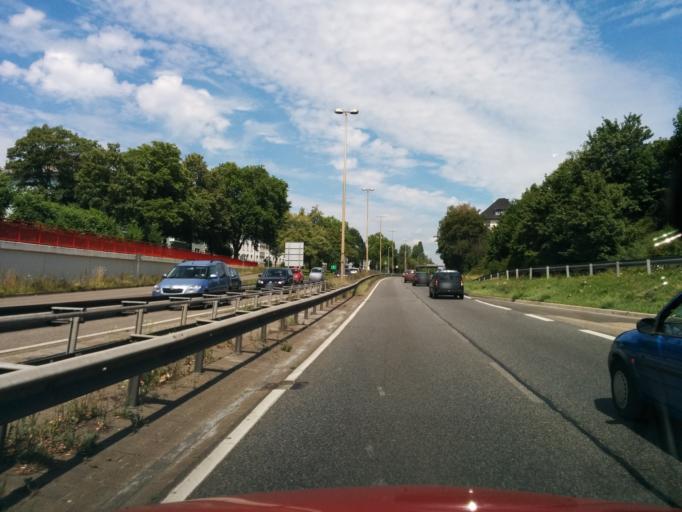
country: DE
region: Rheinland-Pfalz
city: Koblenz
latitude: 50.3696
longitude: 7.5875
